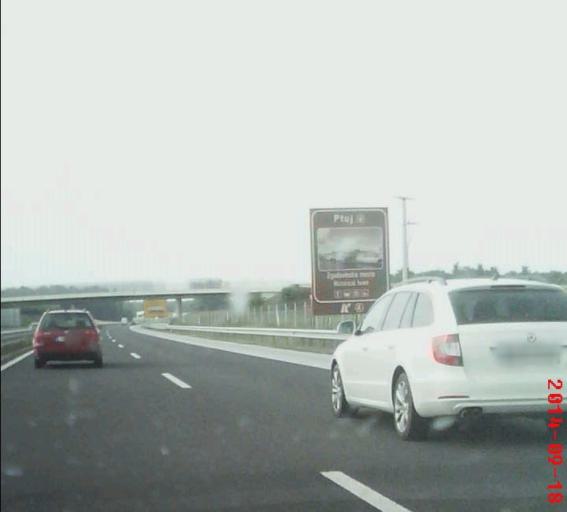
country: SI
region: Hajdina
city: Spodnja Hajdina
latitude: 46.4047
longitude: 15.8226
